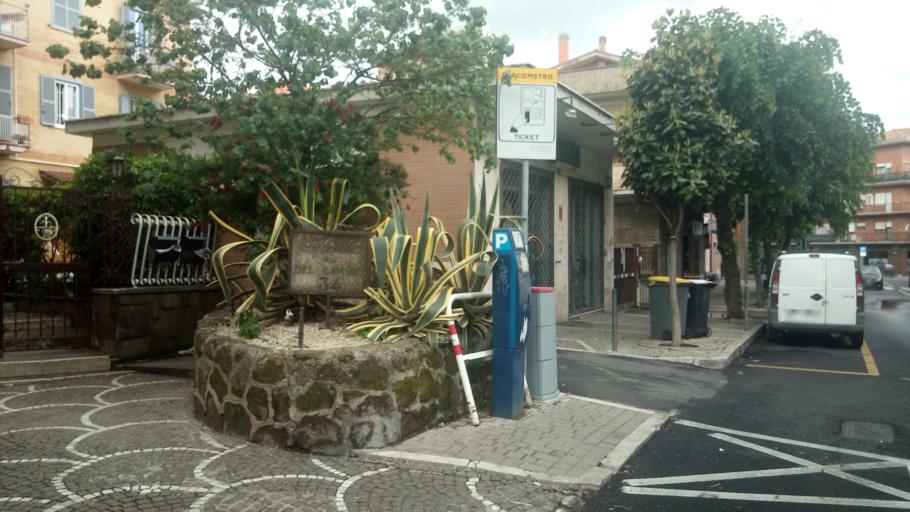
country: IT
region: Latium
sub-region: Citta metropolitana di Roma Capitale
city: Ciampino
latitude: 41.8029
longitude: 12.5992
